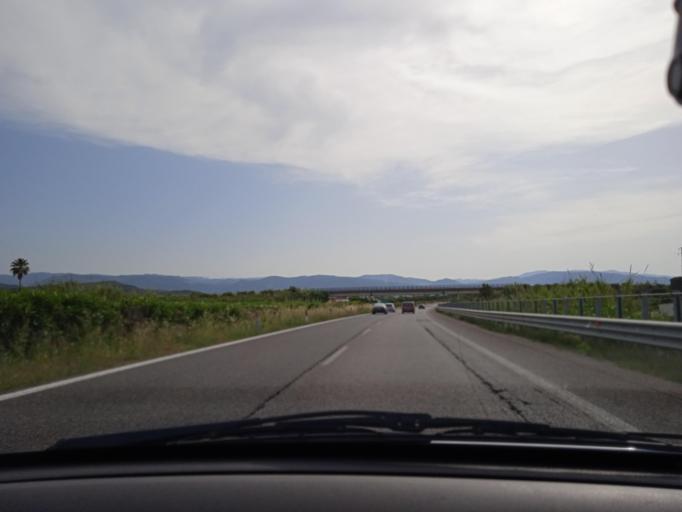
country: IT
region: Sicily
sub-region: Messina
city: Terme
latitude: 38.1358
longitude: 15.1474
